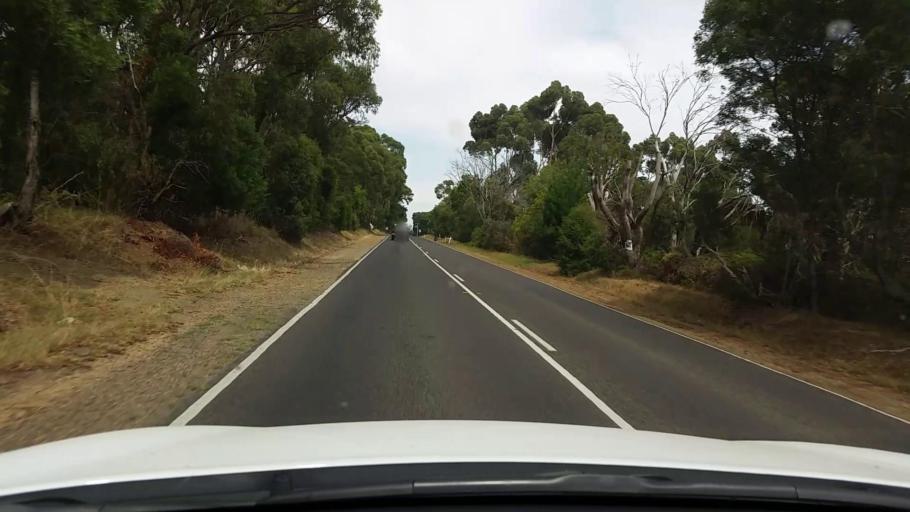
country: AU
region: Victoria
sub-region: Mornington Peninsula
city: Merricks
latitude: -38.3861
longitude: 145.0994
